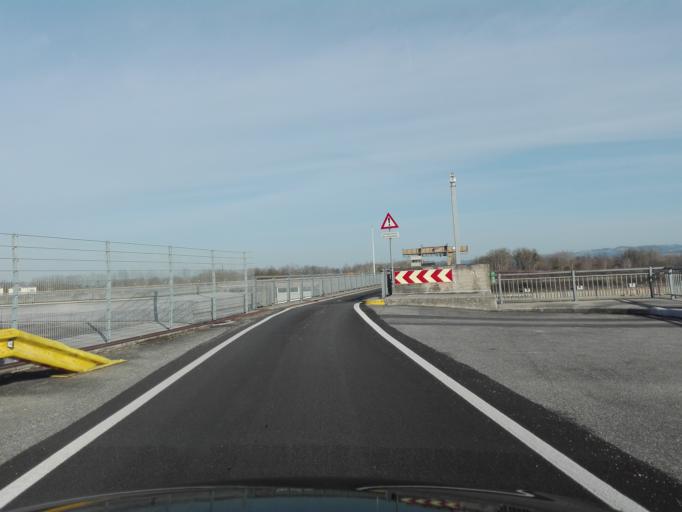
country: AT
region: Lower Austria
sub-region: Politischer Bezirk Amstetten
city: Strengberg
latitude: 48.1671
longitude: 14.6951
